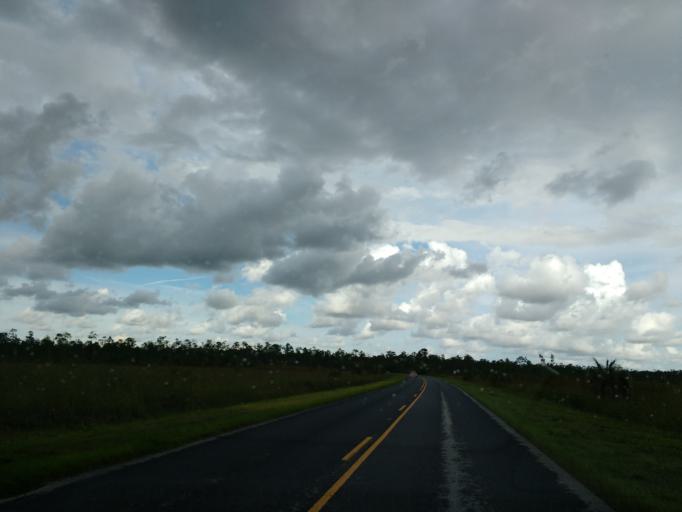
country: US
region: Florida
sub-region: Miami-Dade County
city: Florida City
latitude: 25.3961
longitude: -80.5951
